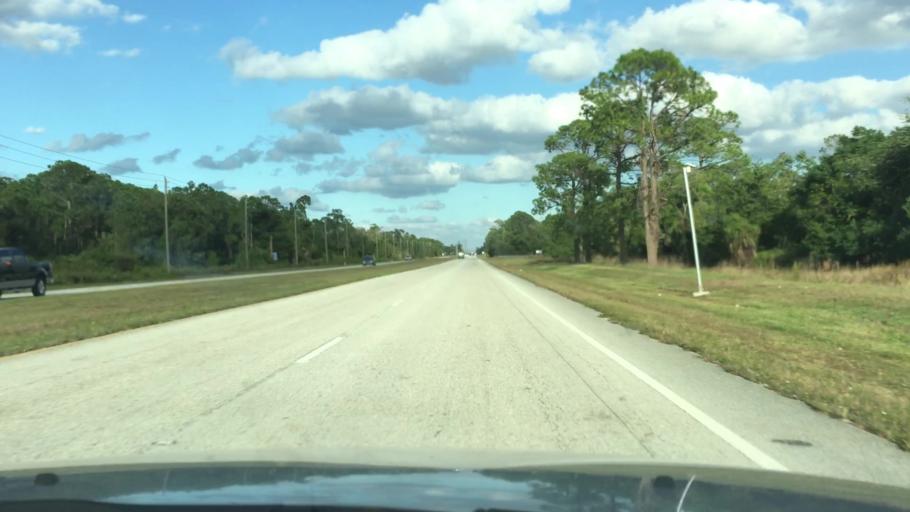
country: US
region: Florida
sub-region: Volusia County
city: Holly Hill
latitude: 29.2286
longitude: -81.0825
